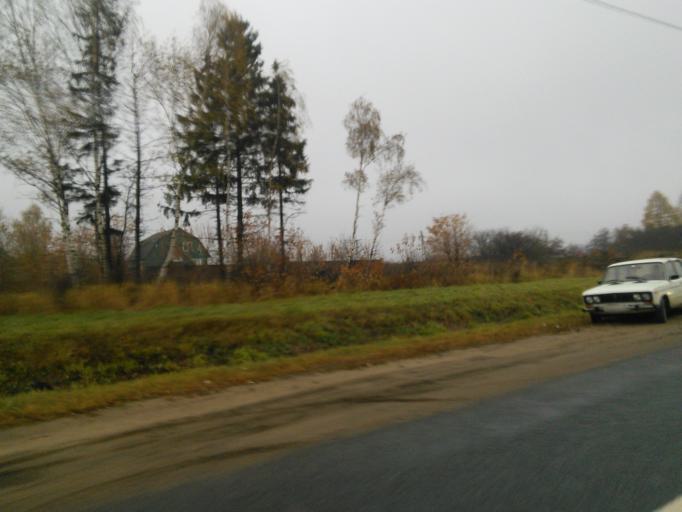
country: RU
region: Jaroslavl
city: Petrovsk
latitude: 56.9995
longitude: 39.2437
